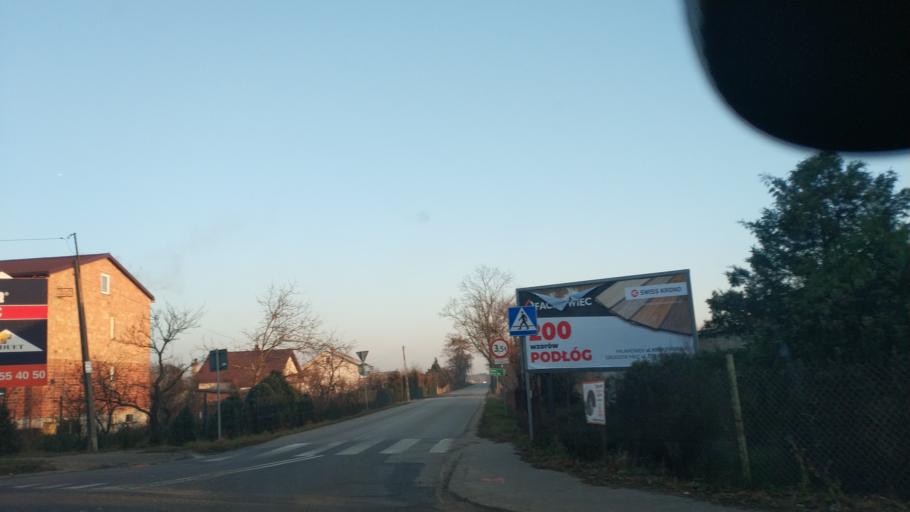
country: PL
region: Masovian Voivodeship
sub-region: Powiat pruszkowski
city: Owczarnia
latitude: 52.0736
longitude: 20.7020
